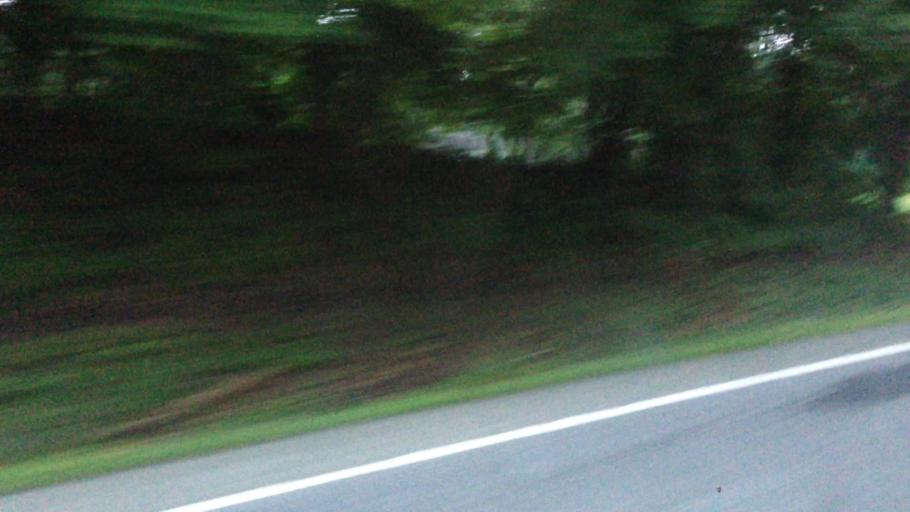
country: US
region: New York
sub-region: Dutchess County
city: Red Hook
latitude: 41.9994
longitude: -73.8999
